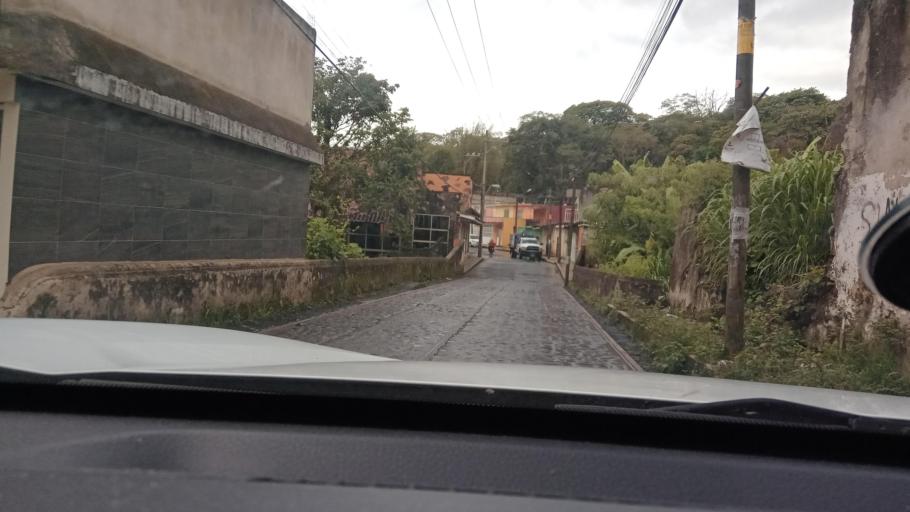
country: MX
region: Veracruz
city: Coatepec
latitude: 19.4462
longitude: -96.9589
